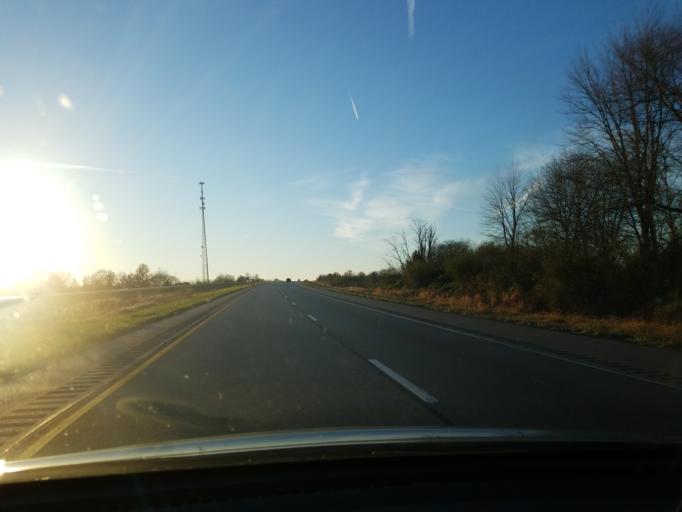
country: US
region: Indiana
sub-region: Gibson County
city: Haubstadt
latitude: 38.1700
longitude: -87.4345
